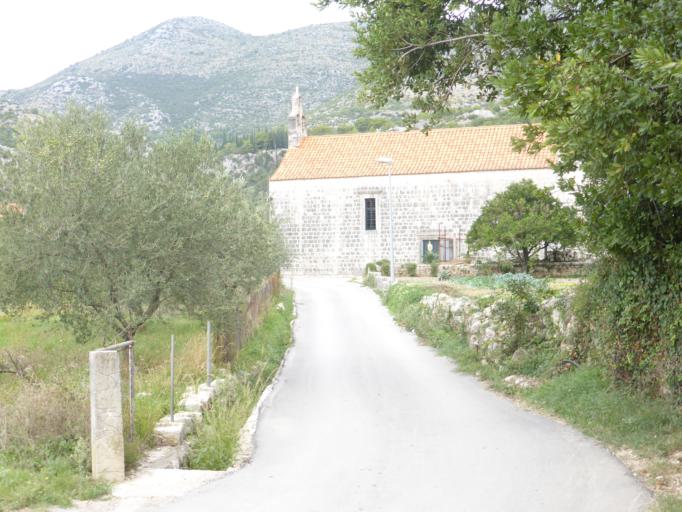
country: HR
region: Dubrovacko-Neretvanska
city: Podgora
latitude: 42.7833
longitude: 17.8902
